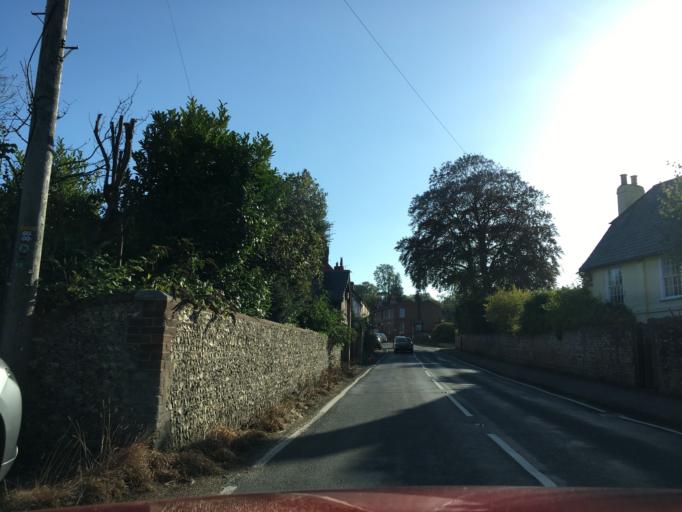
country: GB
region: England
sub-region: Hampshire
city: Swanmore
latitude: 50.9605
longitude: -1.1380
